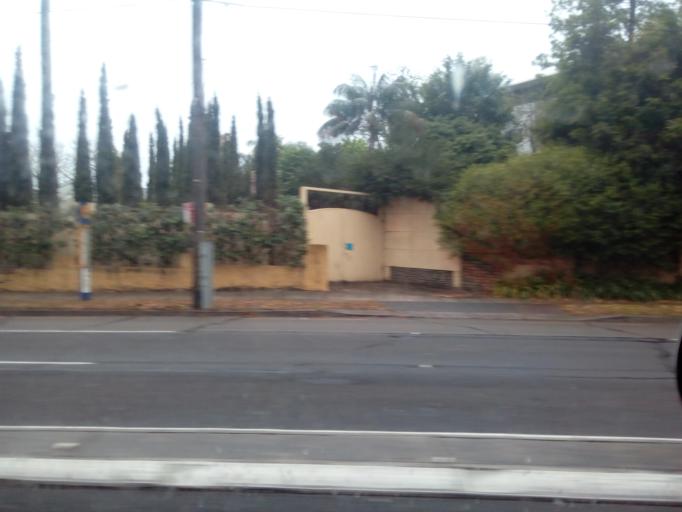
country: AU
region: New South Wales
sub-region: City of Sydney
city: Pymble
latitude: -33.7381
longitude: 151.1352
